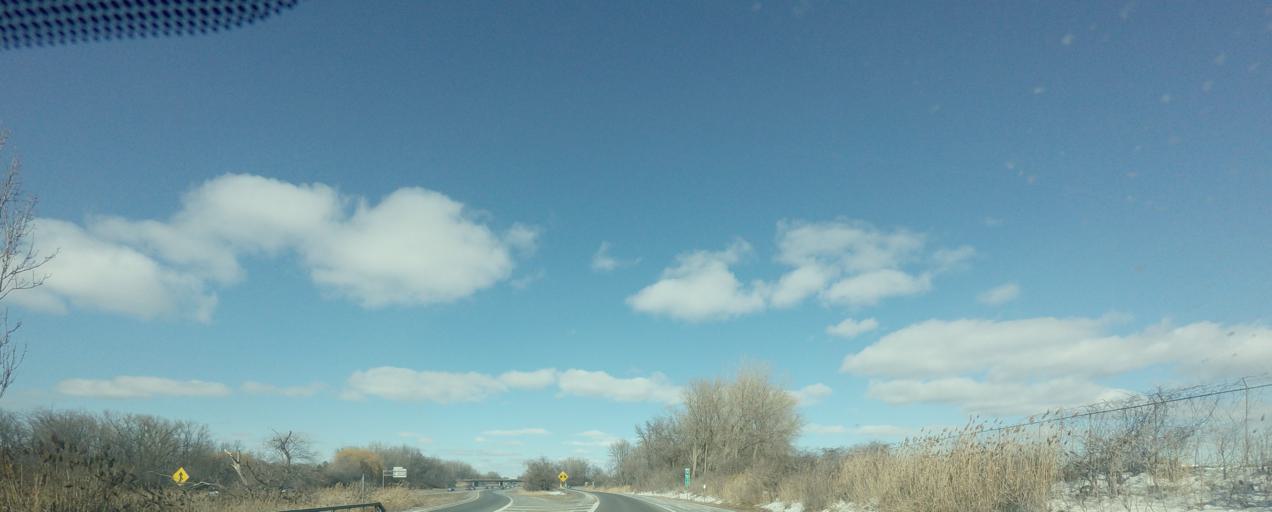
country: US
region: New York
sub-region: Onondaga County
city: North Syracuse
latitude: 43.1195
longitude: -76.1276
